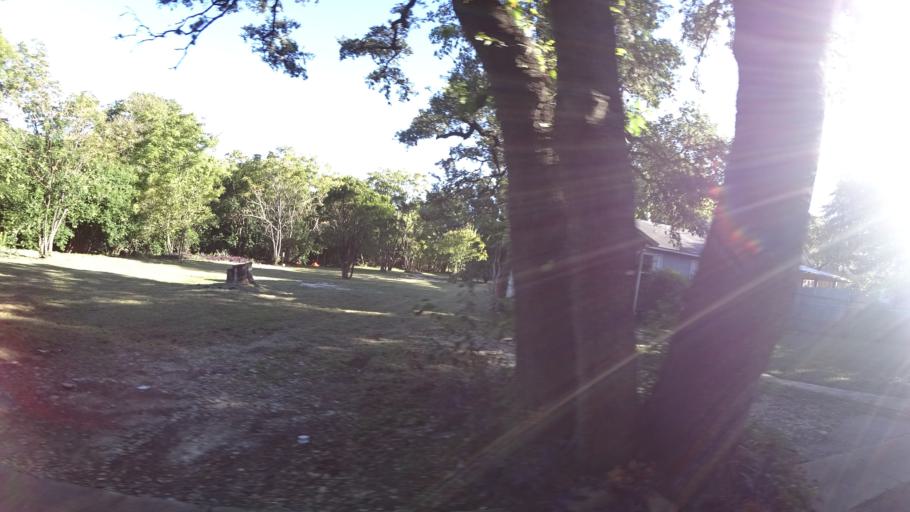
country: US
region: Texas
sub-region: Travis County
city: Austin
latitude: 30.2269
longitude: -97.7645
